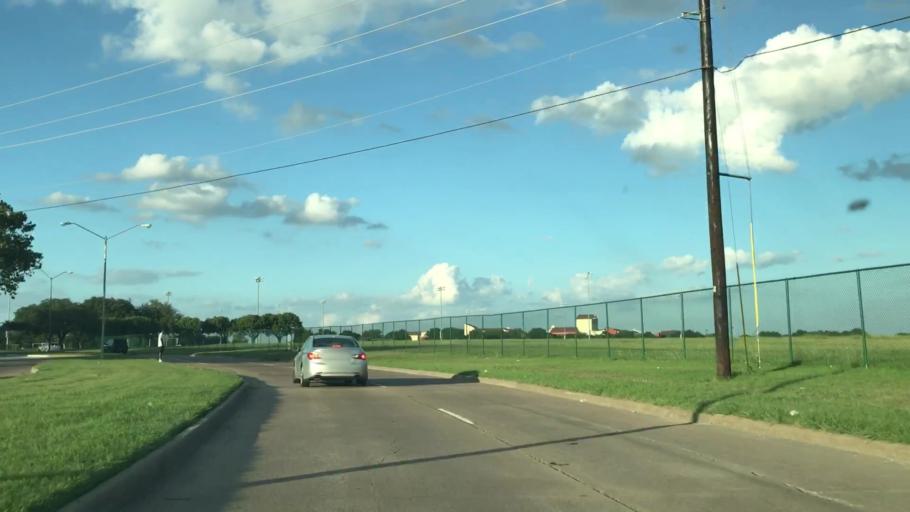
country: US
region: Texas
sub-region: Dallas County
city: Mesquite
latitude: 32.8103
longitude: -96.6656
